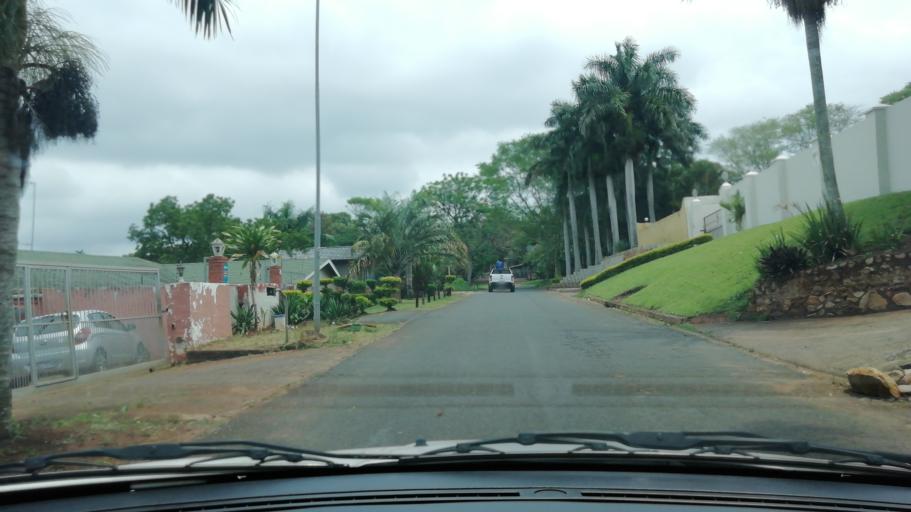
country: ZA
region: KwaZulu-Natal
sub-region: uThungulu District Municipality
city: Empangeni
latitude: -28.7515
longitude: 31.8880
